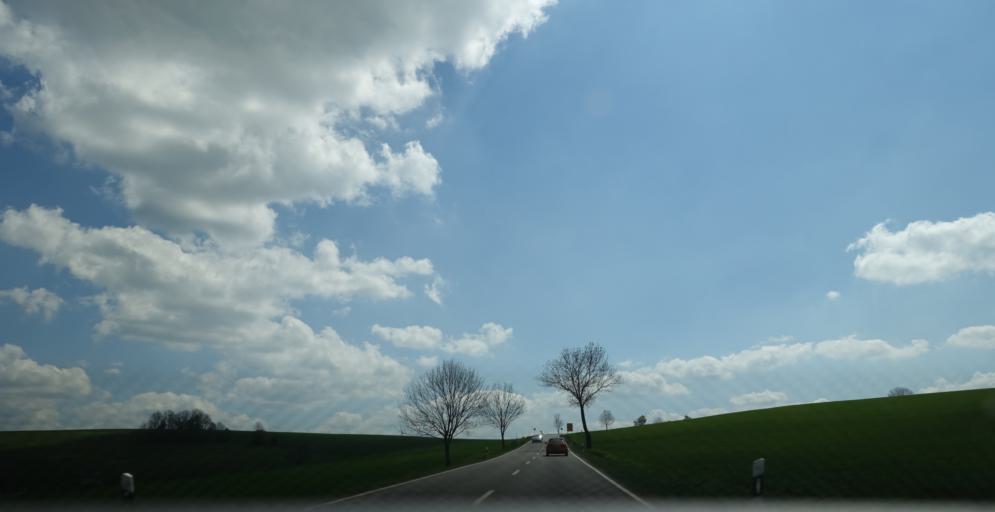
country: DE
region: Saxony
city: Grosshartmannsdorf
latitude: 50.7815
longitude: 13.3218
